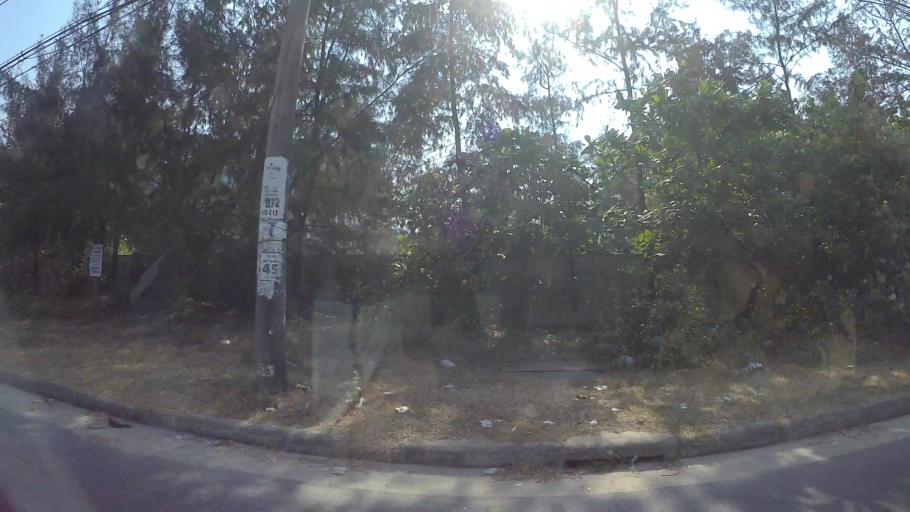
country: VN
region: Da Nang
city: Ngu Hanh Son
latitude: 15.9687
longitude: 108.2836
